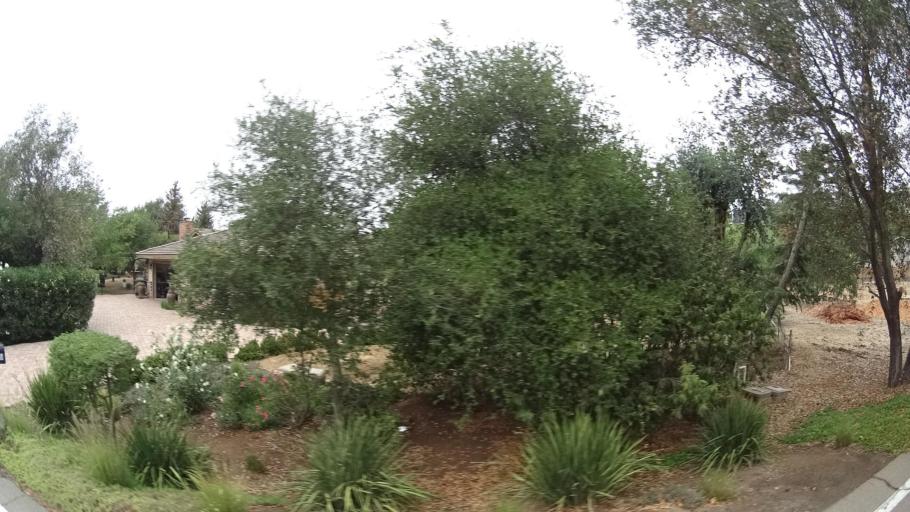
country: US
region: California
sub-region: San Diego County
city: Escondido
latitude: 33.1138
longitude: -117.1266
